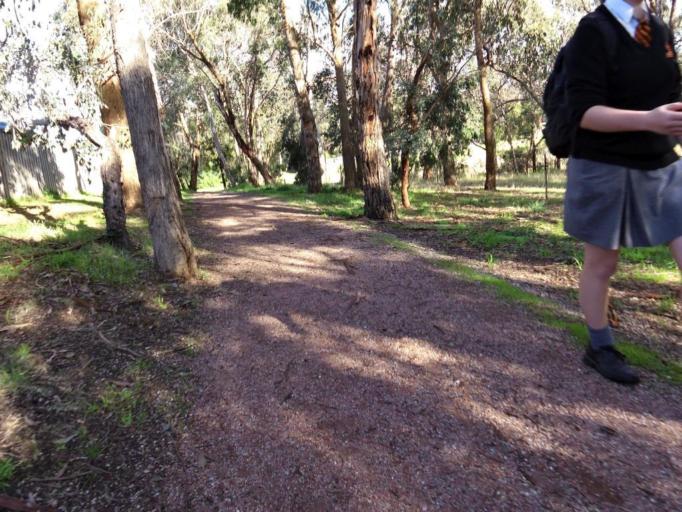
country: AU
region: Victoria
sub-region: Maroondah
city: Croydon Hills
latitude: -37.7773
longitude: 145.2613
